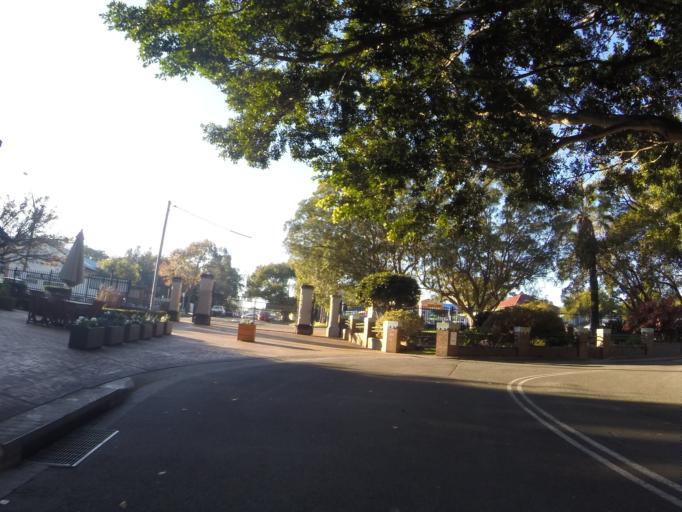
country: AU
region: New South Wales
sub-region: Sutherland Shire
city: Loftus
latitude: -34.0316
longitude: 151.0543
